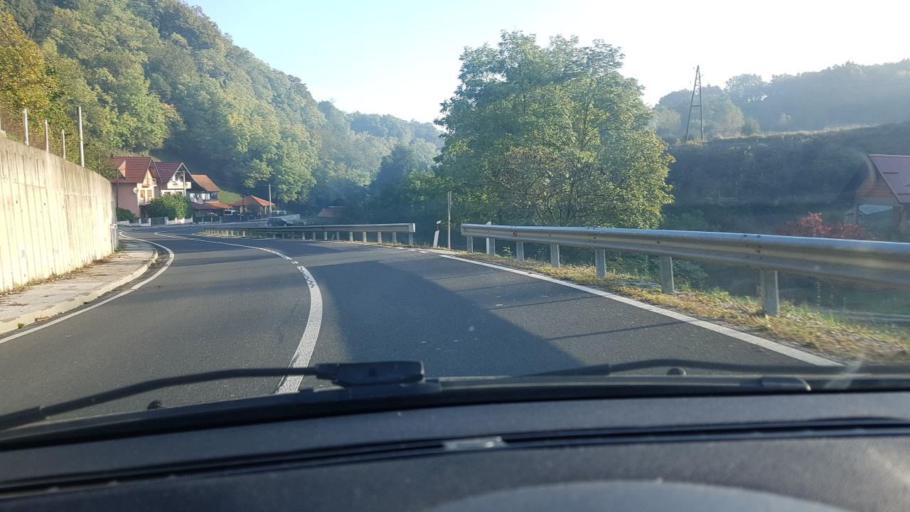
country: HR
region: Krapinsko-Zagorska
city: Marija Bistrica
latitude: 45.9809
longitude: 16.1093
